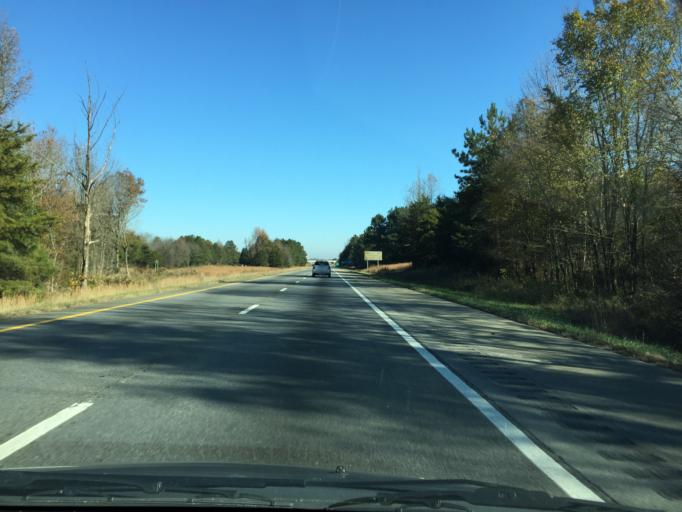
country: US
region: Tennessee
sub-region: Monroe County
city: Sweetwater
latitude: 35.5879
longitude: -84.5255
